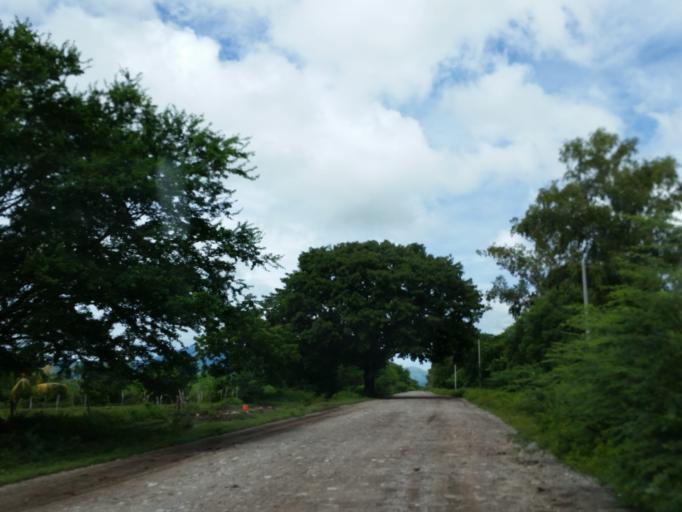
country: NI
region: Leon
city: Telica
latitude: 12.6663
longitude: -86.7905
